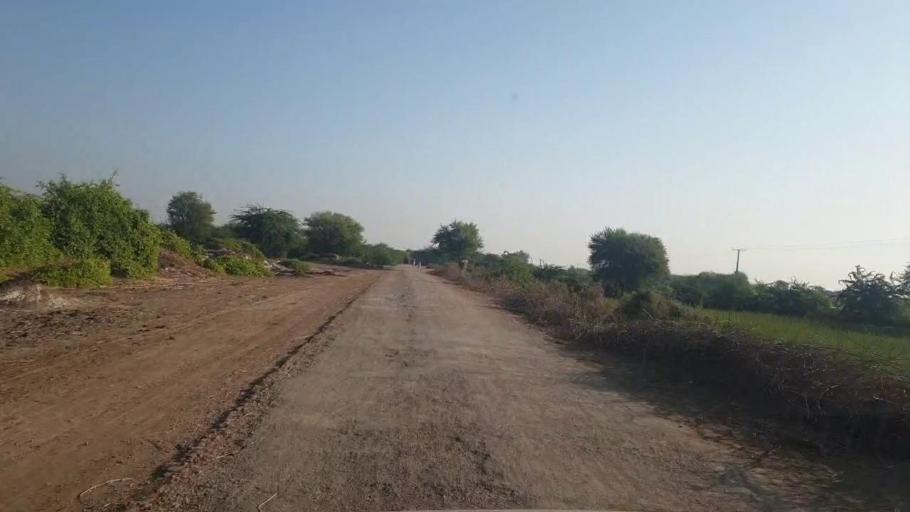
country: PK
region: Sindh
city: Tando Bago
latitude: 24.7379
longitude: 68.8875
